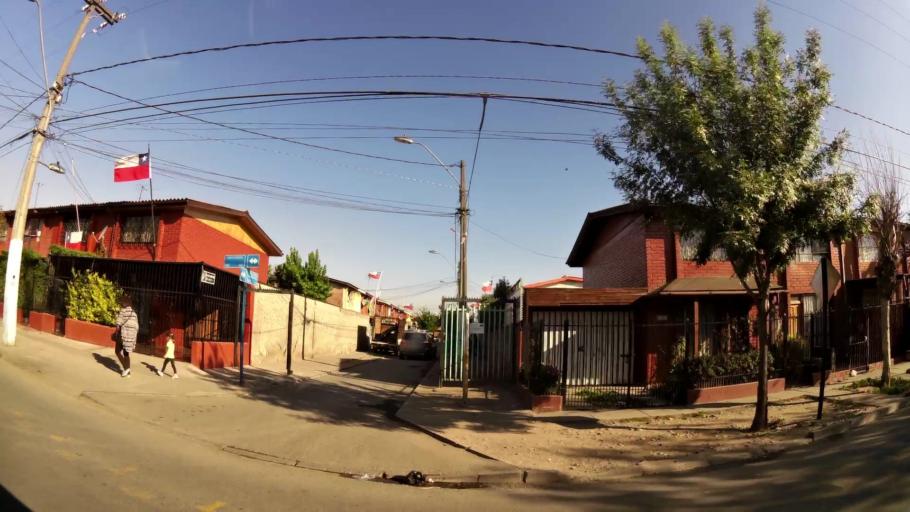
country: CL
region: Santiago Metropolitan
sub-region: Provincia de Santiago
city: La Pintana
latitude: -33.5507
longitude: -70.6258
